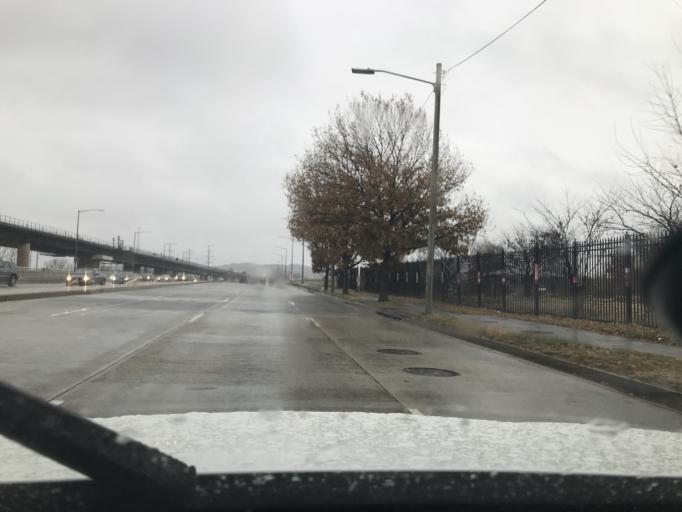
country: US
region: Maryland
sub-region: Prince George's County
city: Colmar Manor
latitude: 38.8971
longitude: -76.9639
